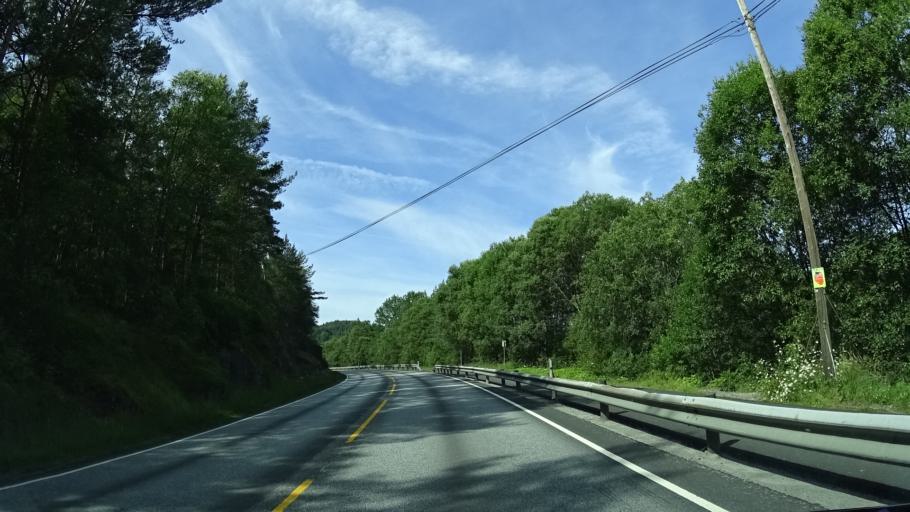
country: NO
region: Hordaland
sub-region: Sveio
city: Sveio
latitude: 59.5794
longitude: 5.4259
